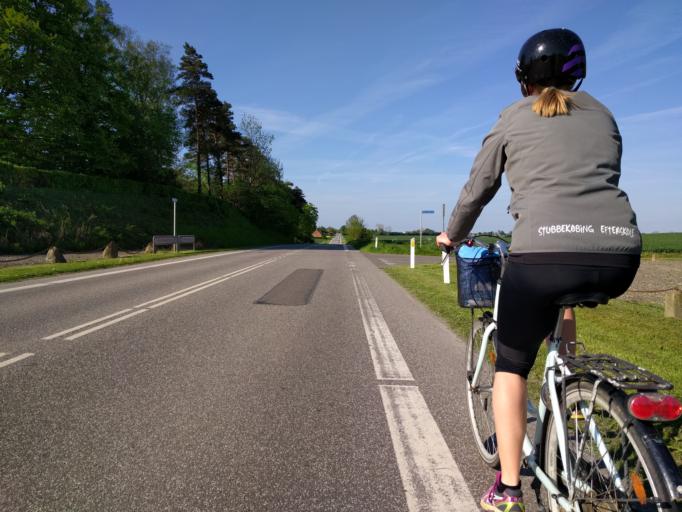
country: DK
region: Zealand
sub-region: Guldborgsund Kommune
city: Stubbekobing
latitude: 54.8470
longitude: 12.0108
